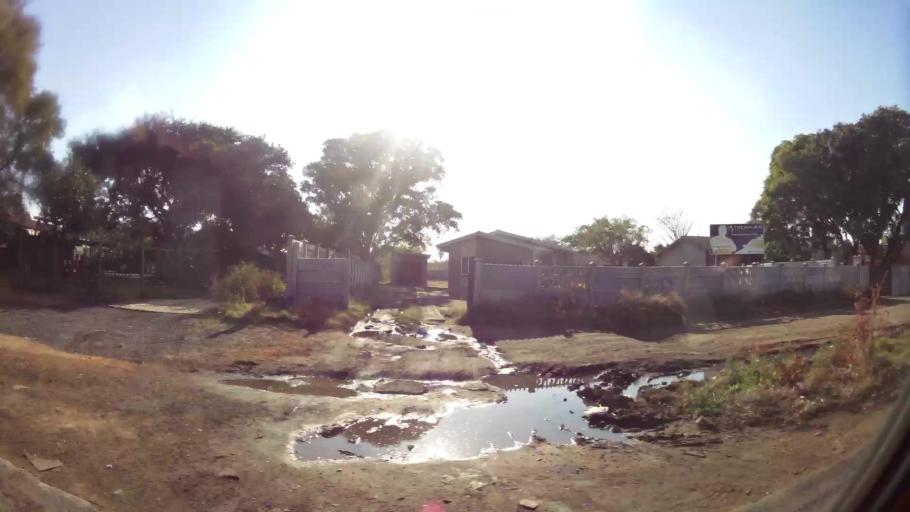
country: ZA
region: North-West
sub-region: Bojanala Platinum District Municipality
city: Rustenburg
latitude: -25.6550
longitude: 27.2299
